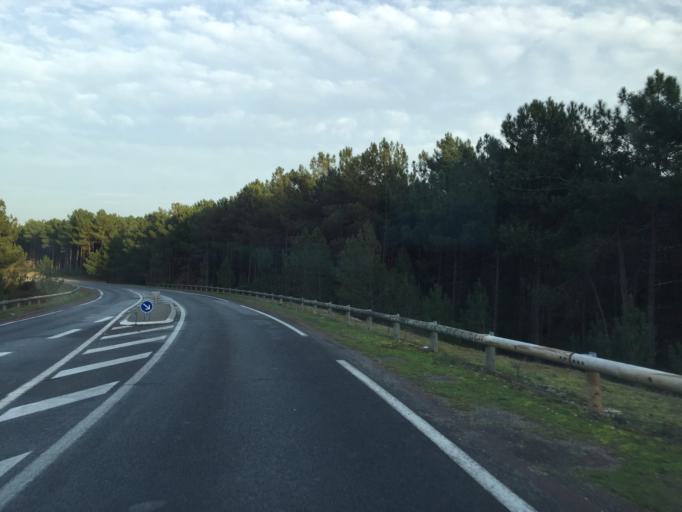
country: FR
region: Aquitaine
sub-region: Departement de la Gironde
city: Lacanau
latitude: 45.0035
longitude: -1.1517
